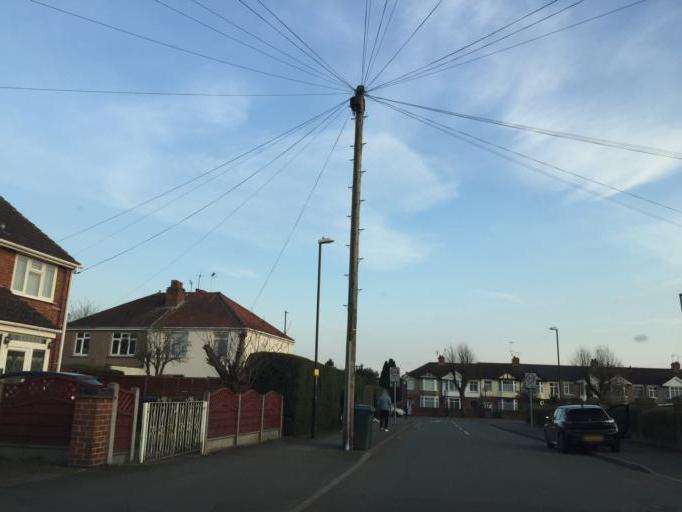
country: GB
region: England
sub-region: Coventry
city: Coventry
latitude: 52.4042
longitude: -1.5647
